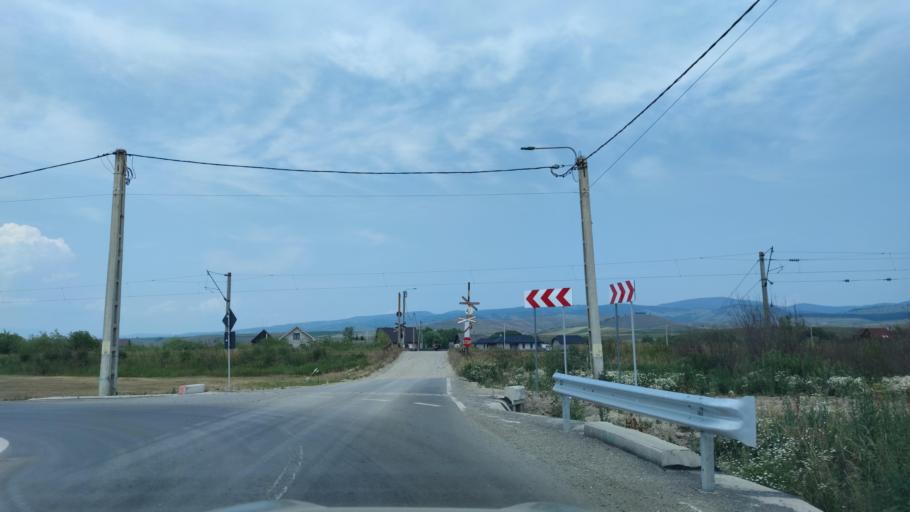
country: RO
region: Harghita
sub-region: Comuna Remetea
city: Remetea
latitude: 46.8152
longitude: 25.4607
